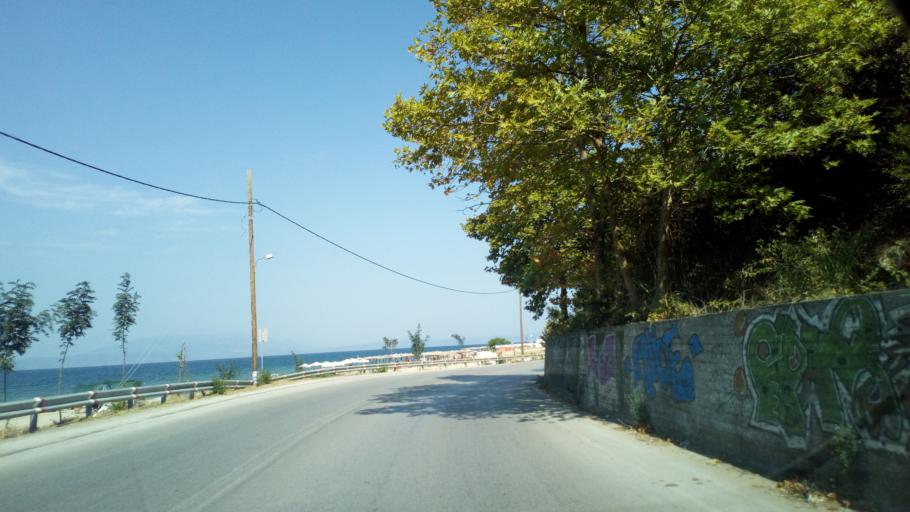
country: GR
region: Central Macedonia
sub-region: Nomos Thessalonikis
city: Stavros
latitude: 40.6628
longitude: 23.7095
